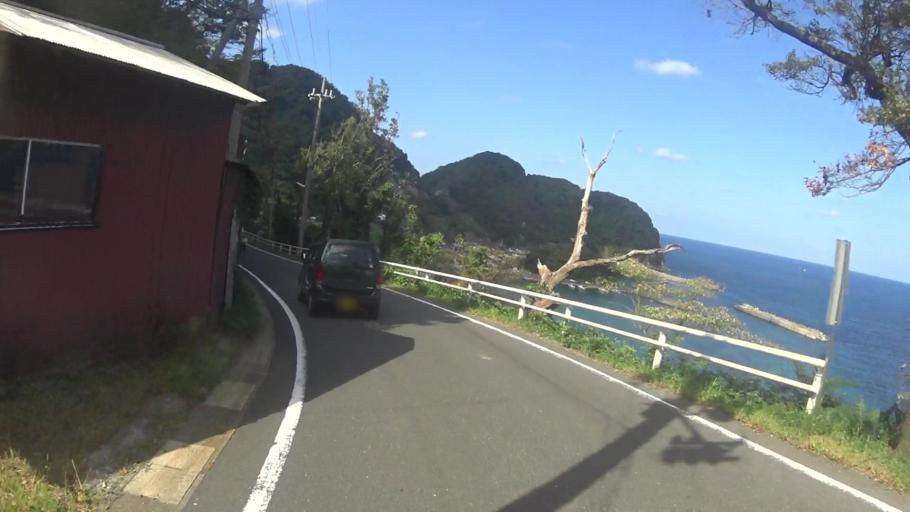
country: JP
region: Kyoto
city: Miyazu
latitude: 35.7491
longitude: 135.2512
